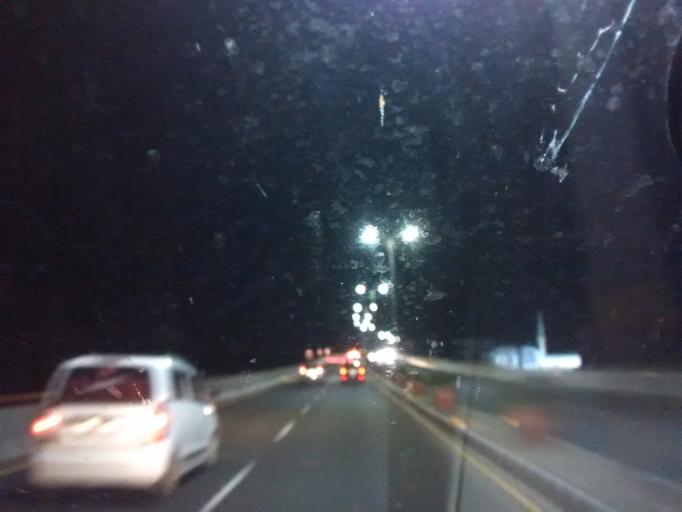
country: IN
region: Telangana
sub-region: Hyderabad
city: Hyderabad
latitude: 17.3424
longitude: 78.4208
